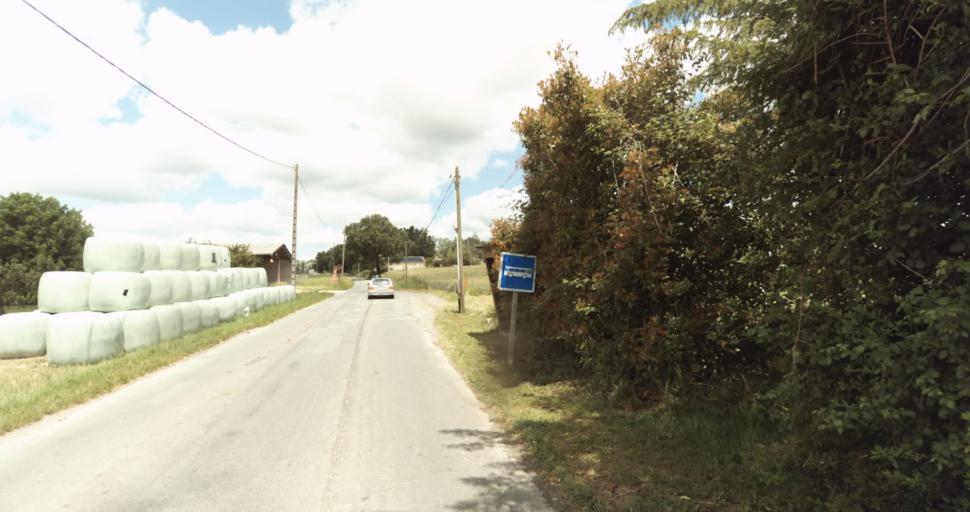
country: FR
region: Aquitaine
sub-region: Departement de la Dordogne
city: Beaumont-du-Perigord
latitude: 44.7263
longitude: 0.7581
